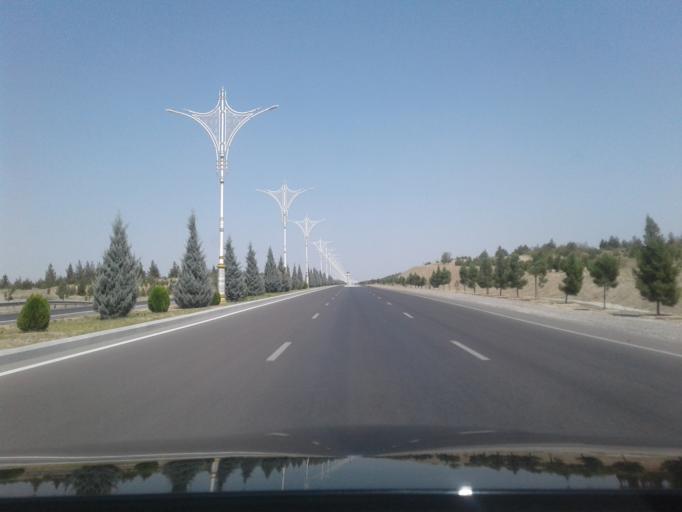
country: TM
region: Ahal
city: Ashgabat
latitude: 37.8784
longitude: 58.4020
